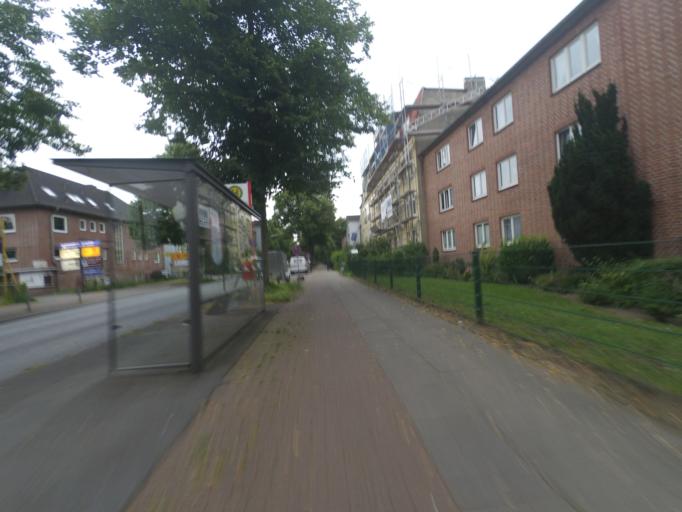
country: DE
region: Hamburg
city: Bergedorf
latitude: 53.4891
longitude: 10.1933
